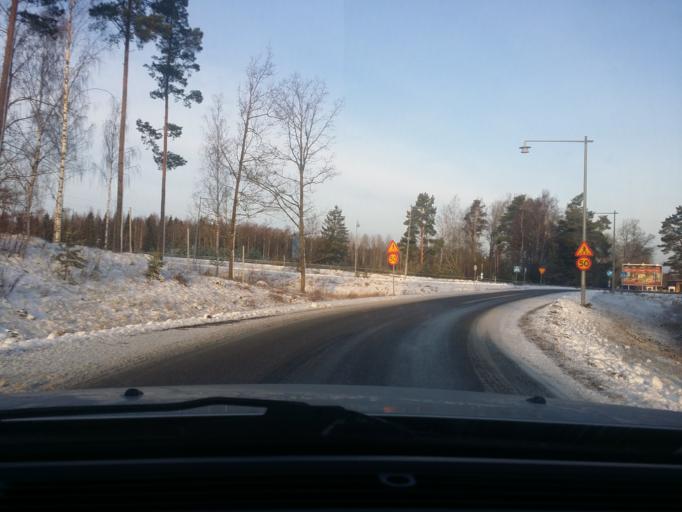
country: SE
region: Vaestmanland
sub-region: Arboga Kommun
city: Arboga
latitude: 59.4254
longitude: 15.8271
